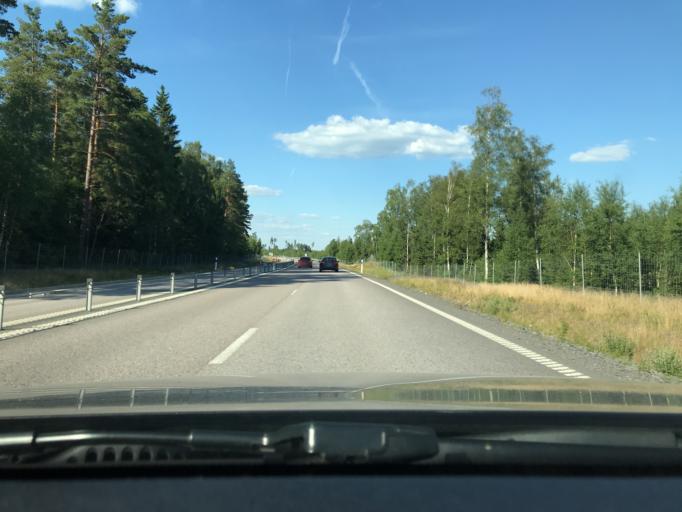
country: SE
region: Kronoberg
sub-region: Alvesta Kommun
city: Vislanda
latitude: 56.6651
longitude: 14.3036
